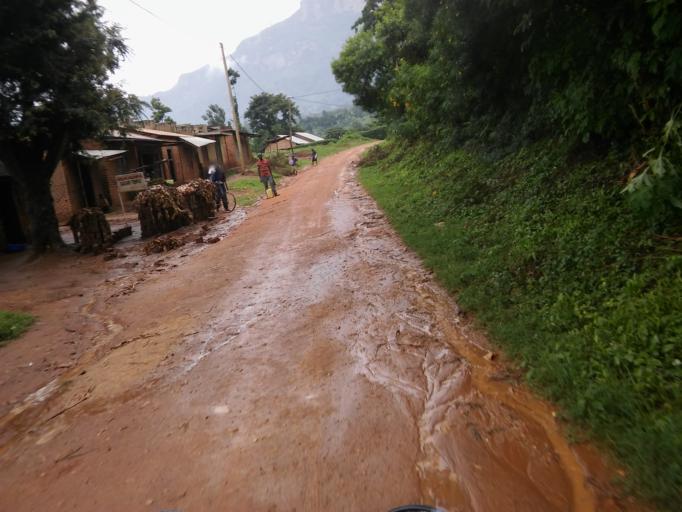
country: UG
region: Eastern Region
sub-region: Bududa District
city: Bududa
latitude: 0.9925
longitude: 34.2327
